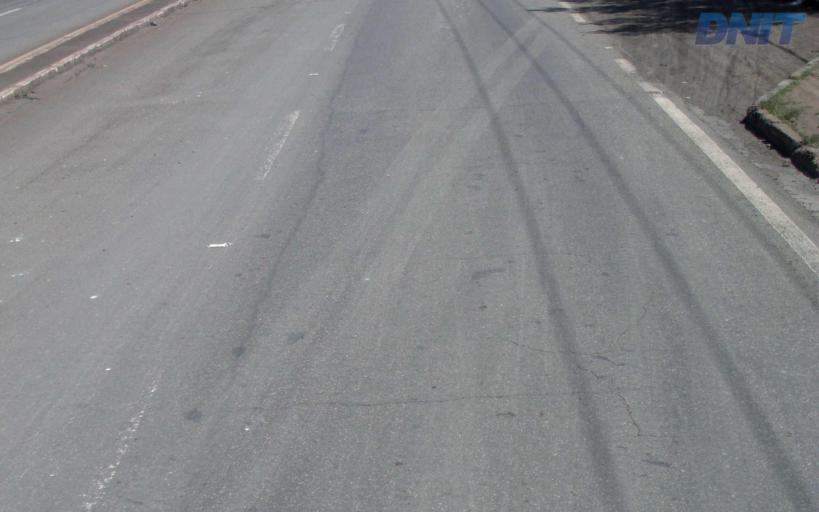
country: BR
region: Minas Gerais
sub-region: Coronel Fabriciano
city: Coronel Fabriciano
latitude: -19.5283
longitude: -42.6471
